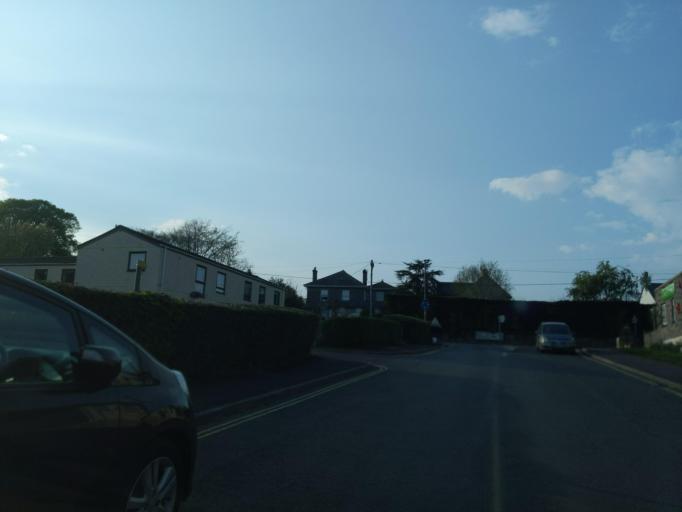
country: GB
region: England
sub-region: Devon
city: Yealmpton
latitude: 50.3500
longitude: -4.0383
